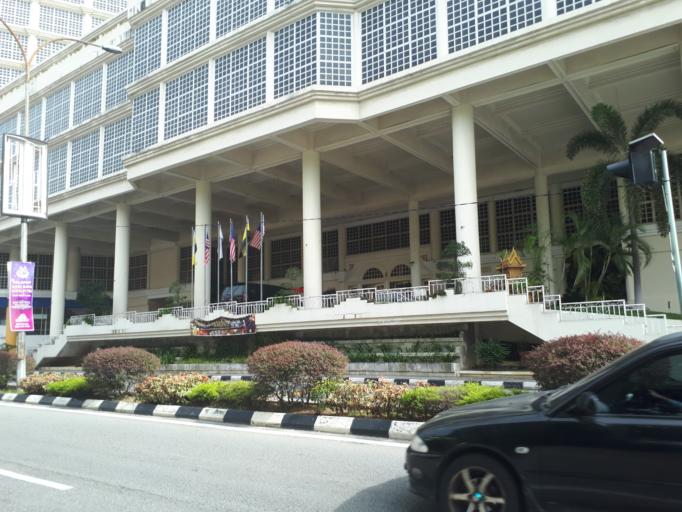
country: MY
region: Perak
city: Ipoh
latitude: 4.5974
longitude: 101.0887
